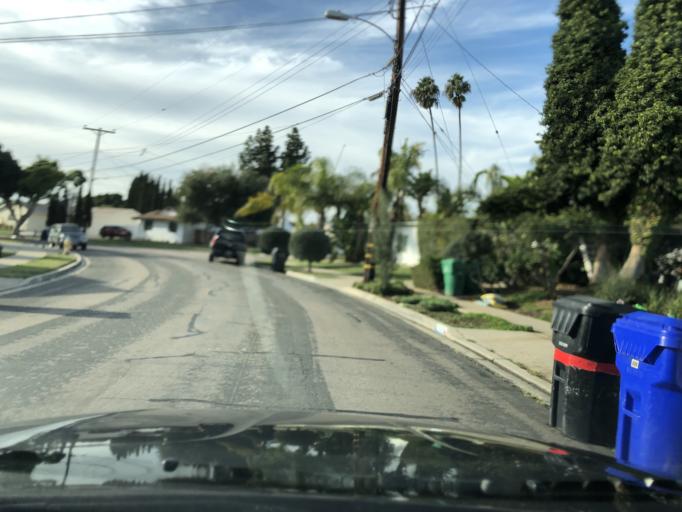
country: US
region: California
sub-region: San Diego County
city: La Jolla
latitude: 32.8254
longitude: -117.1750
